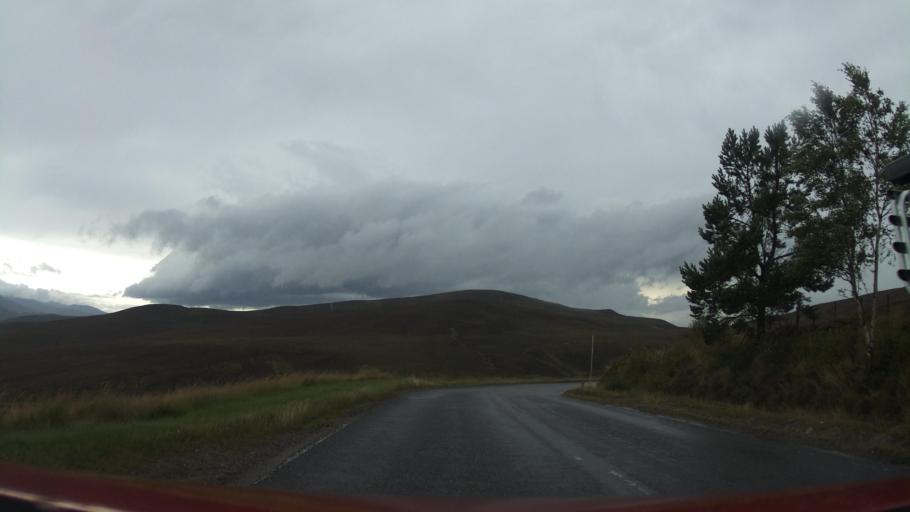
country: GB
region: Scotland
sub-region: Highland
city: Grantown on Spey
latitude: 57.2627
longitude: -3.4856
